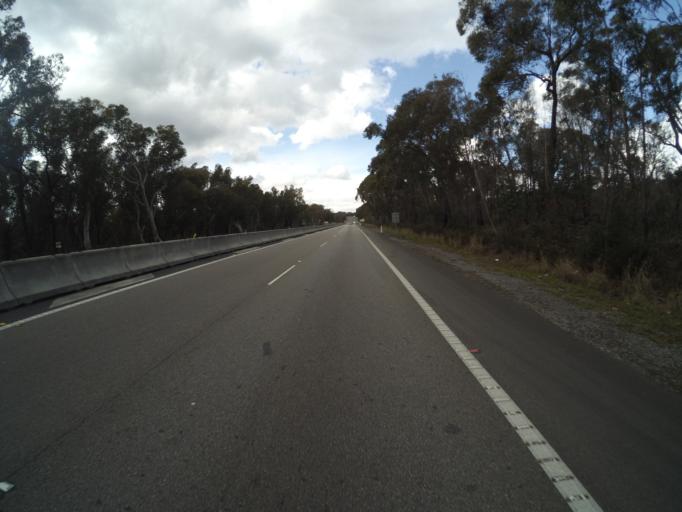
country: AU
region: New South Wales
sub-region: Wollongong
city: Mount Keira
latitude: -34.3252
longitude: 150.7729
